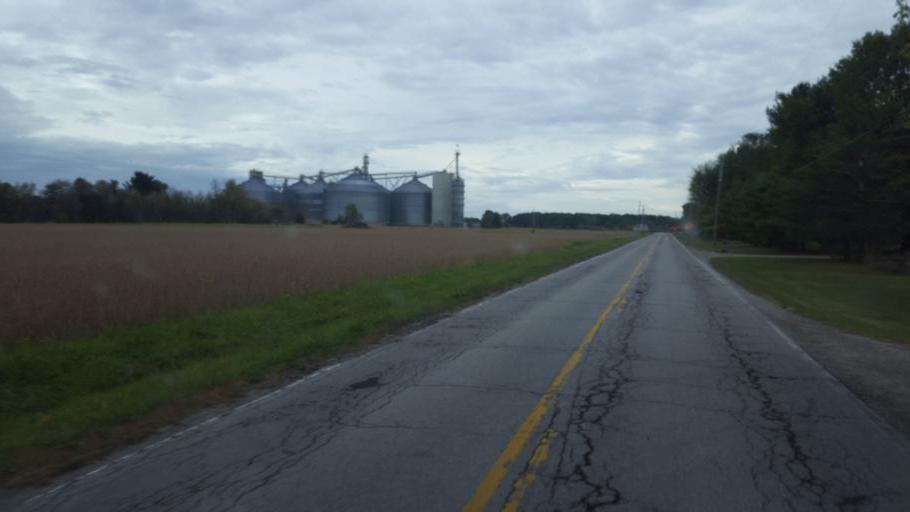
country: US
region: Ohio
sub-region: Huron County
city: Wakeman
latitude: 41.1960
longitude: -82.4236
